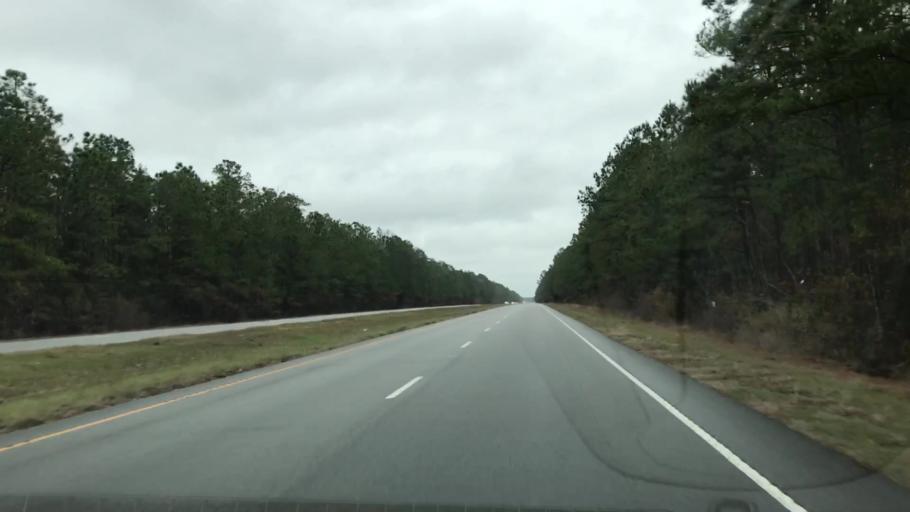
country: US
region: South Carolina
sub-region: Charleston County
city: Awendaw
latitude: 33.1520
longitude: -79.4319
